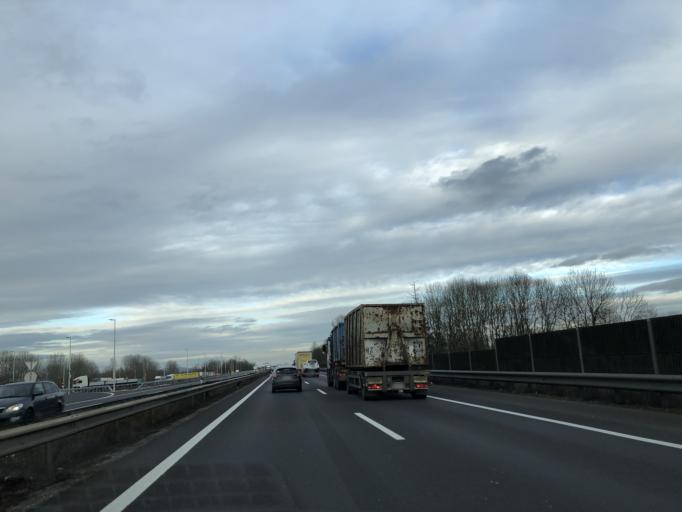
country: AT
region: Upper Austria
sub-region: Wels-Land
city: Marchtrenk
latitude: 48.1850
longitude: 14.1542
